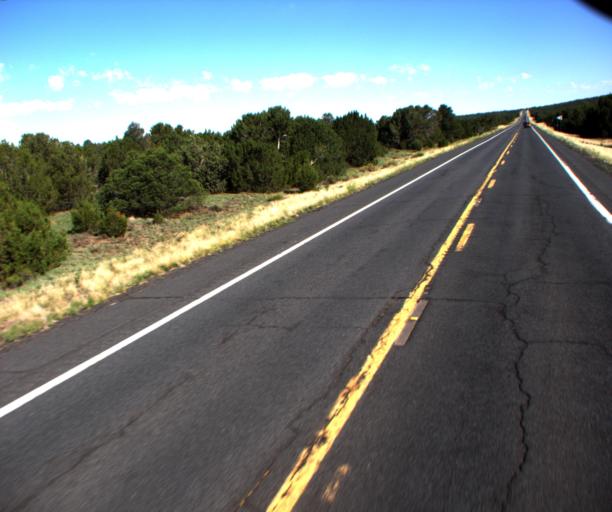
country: US
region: Arizona
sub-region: Coconino County
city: Williams
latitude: 35.3816
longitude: -112.1623
